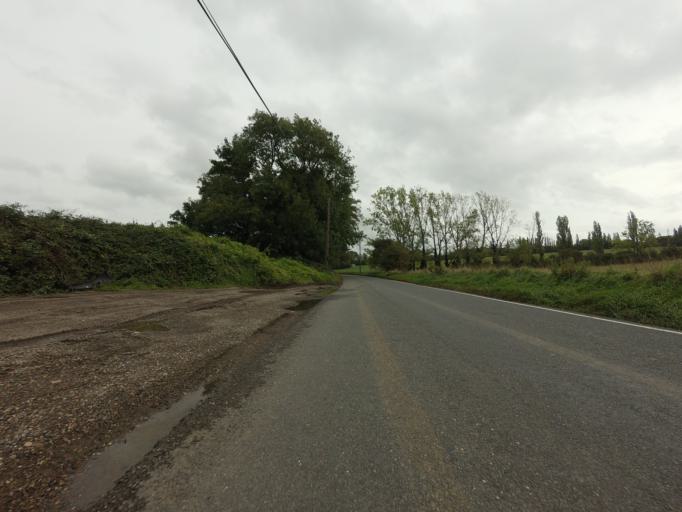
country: GB
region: England
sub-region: Cambridgeshire
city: Duxford
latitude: 52.0197
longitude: 0.1305
